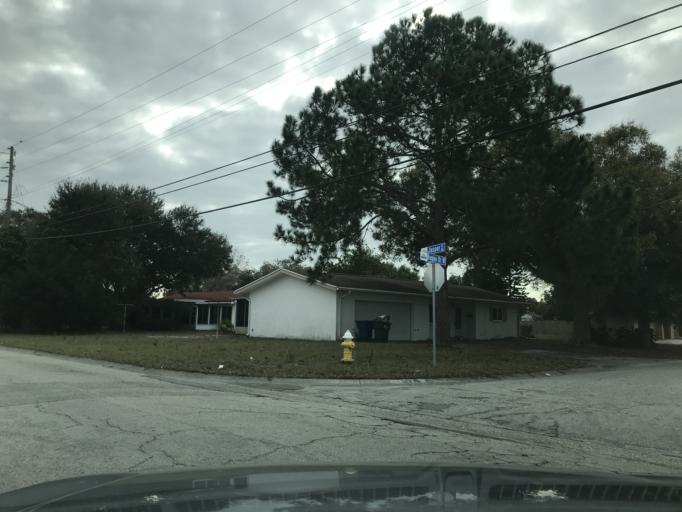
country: US
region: Florida
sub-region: Pinellas County
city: Belleair
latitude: 27.9315
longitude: -82.7859
